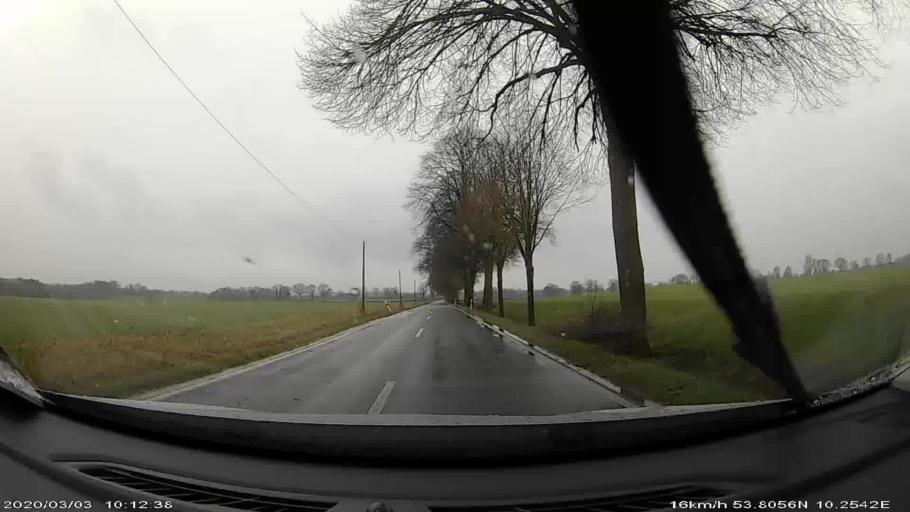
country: DE
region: Schleswig-Holstein
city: Sulfeld
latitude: 53.8050
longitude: 10.2469
